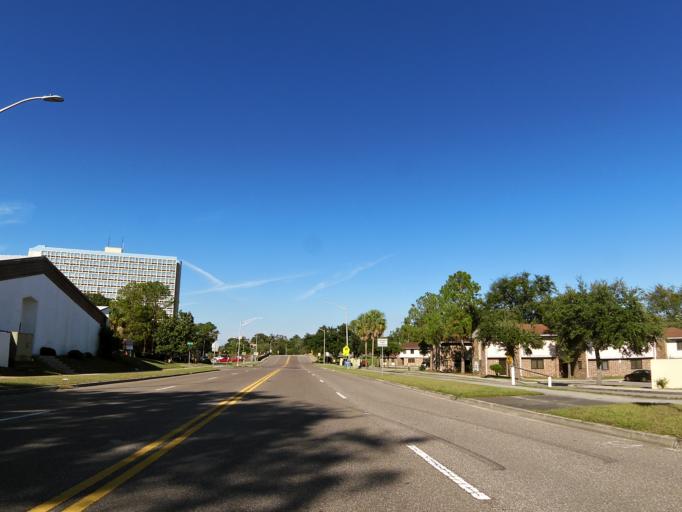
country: US
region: Florida
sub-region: Duval County
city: Jacksonville
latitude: 30.3390
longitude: -81.6621
